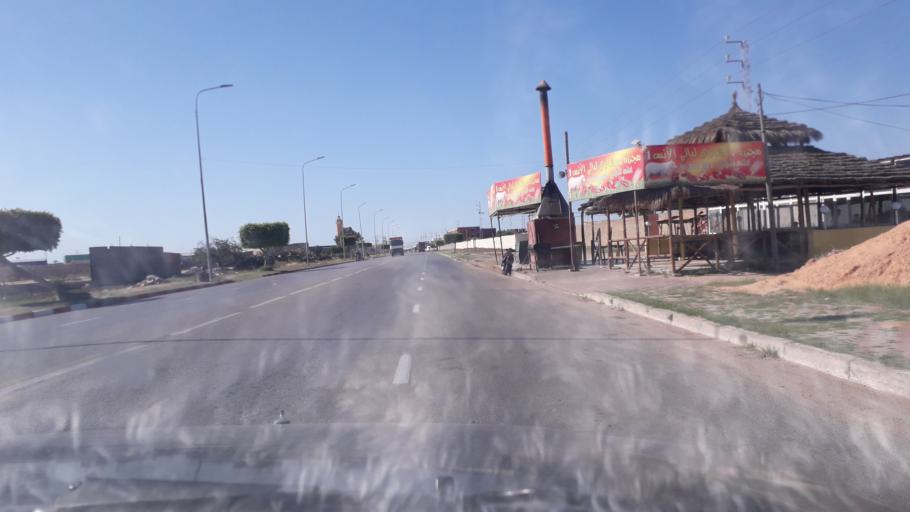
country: TN
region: Safaqis
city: Al Qarmadah
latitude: 34.8539
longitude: 10.7607
